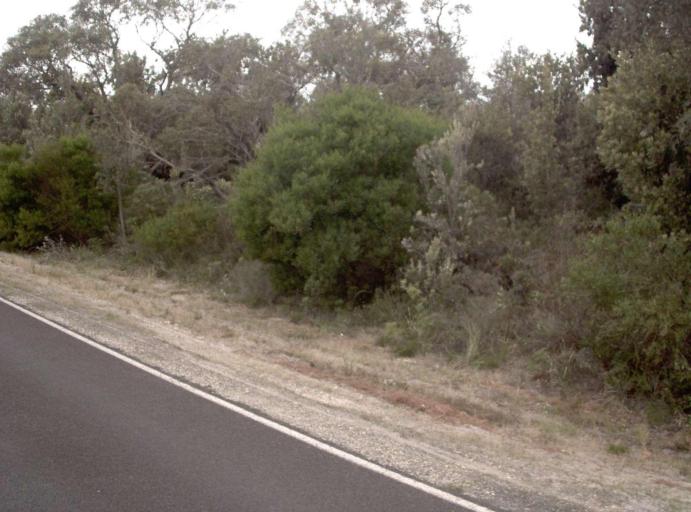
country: AU
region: Victoria
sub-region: East Gippsland
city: Bairnsdale
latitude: -38.0923
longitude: 147.5172
